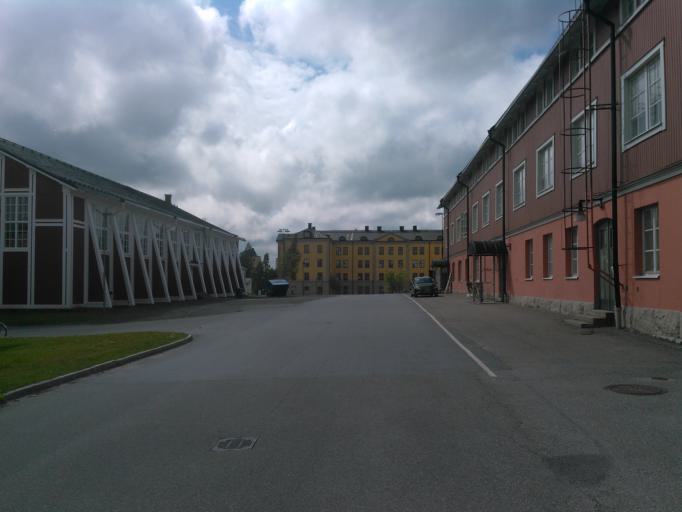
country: SE
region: Vaesterbotten
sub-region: Umea Kommun
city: Umea
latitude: 63.8358
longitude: 20.2623
